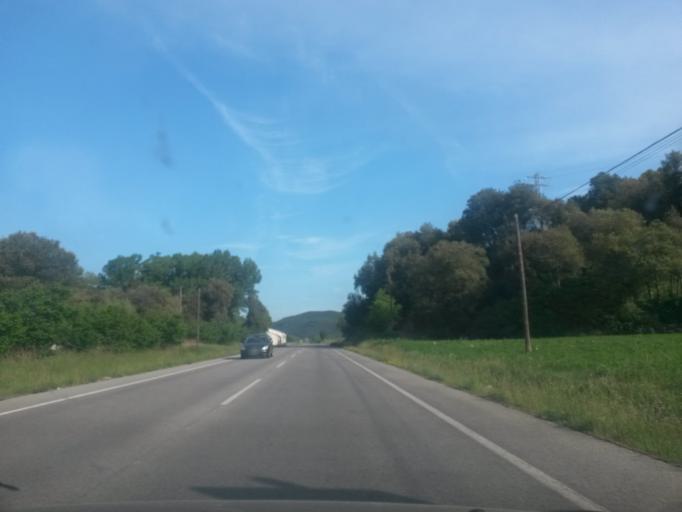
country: ES
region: Catalonia
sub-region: Provincia de Girona
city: les Planes d'Hostoles
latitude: 42.0233
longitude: 2.5910
